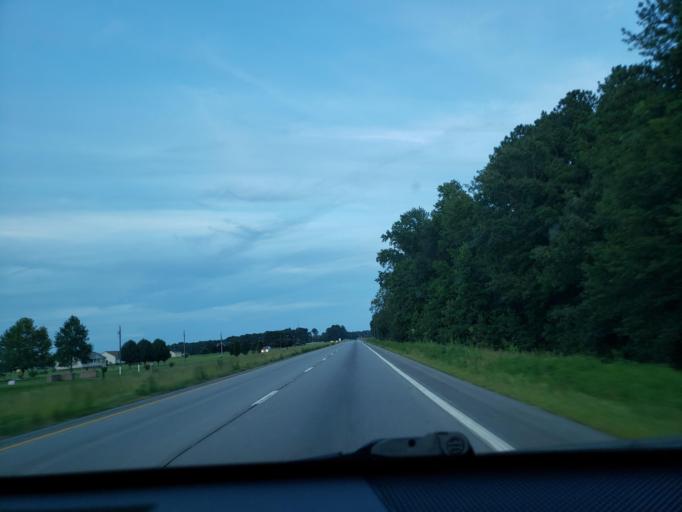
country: US
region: Virginia
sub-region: Southampton County
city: Courtland
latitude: 36.7075
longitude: -77.1484
